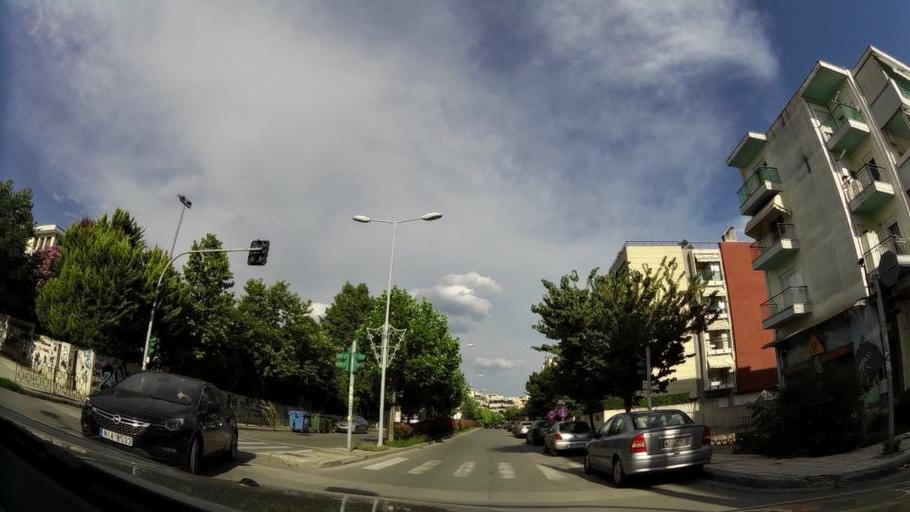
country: GR
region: Central Macedonia
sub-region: Nomos Thessalonikis
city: Kalamaria
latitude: 40.5764
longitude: 22.9621
